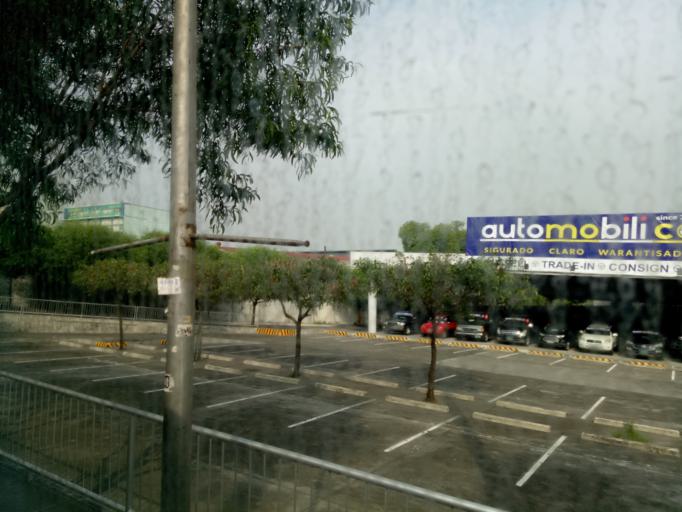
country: PH
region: Calabarzon
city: Bagong Pagasa
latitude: 14.7070
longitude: 121.0386
